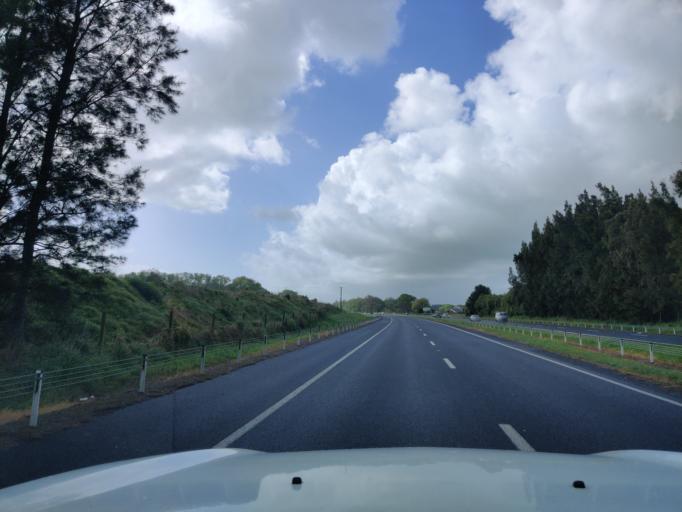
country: NZ
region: Waikato
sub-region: Waipa District
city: Cambridge
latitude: -37.8376
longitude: 175.3670
